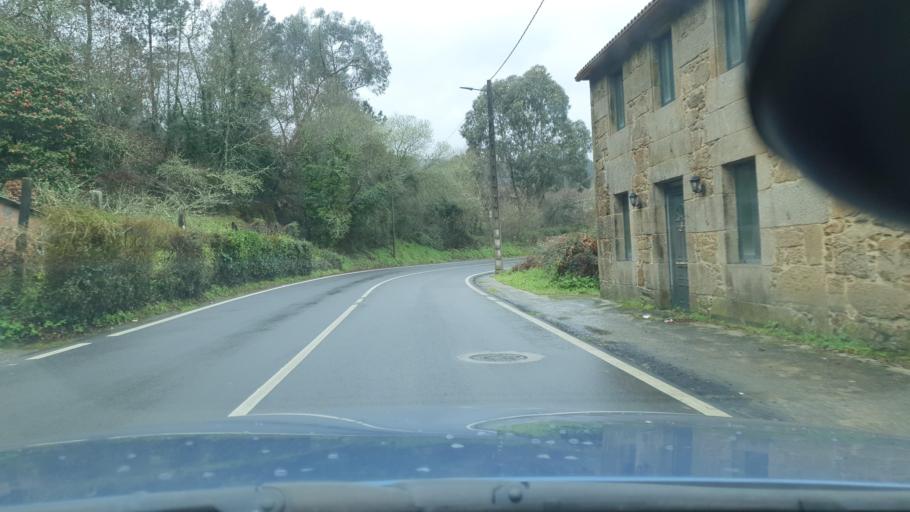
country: ES
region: Galicia
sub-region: Provincia da Coruna
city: Padron
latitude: 42.7501
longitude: -8.6718
